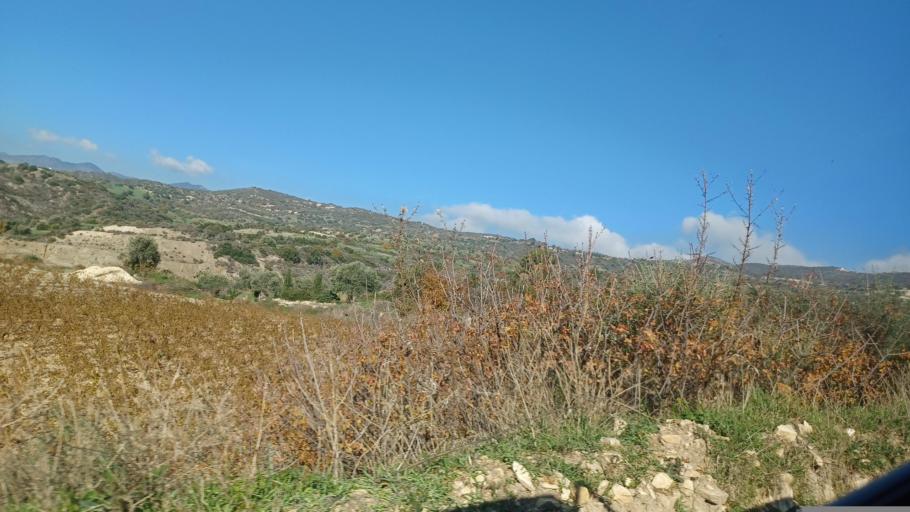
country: CY
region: Larnaka
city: Kofinou
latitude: 34.8430
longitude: 33.2950
